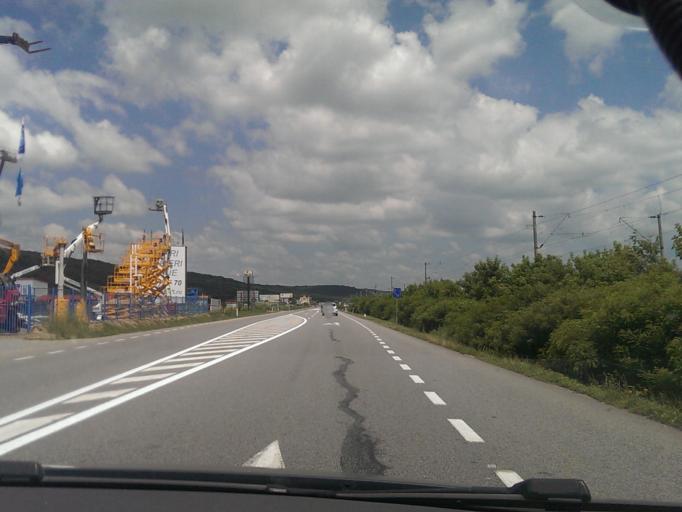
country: RO
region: Cluj
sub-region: Comuna Apahida
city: Apahida
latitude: 46.8279
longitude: 23.7452
